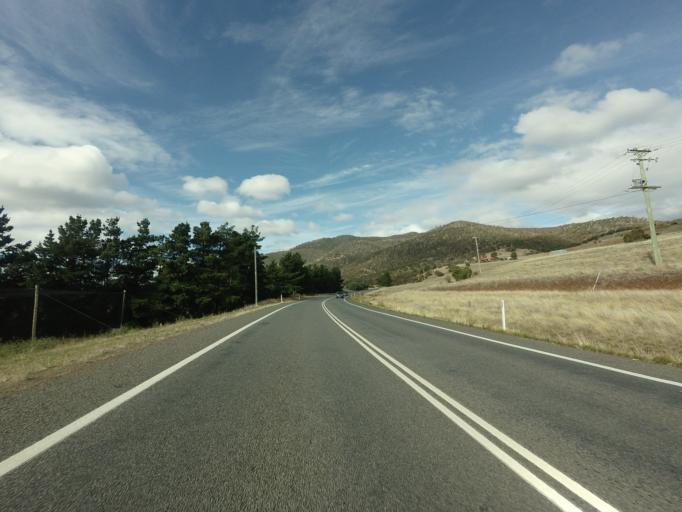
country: AU
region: Tasmania
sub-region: Derwent Valley
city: New Norfolk
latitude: -42.7733
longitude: 147.1233
